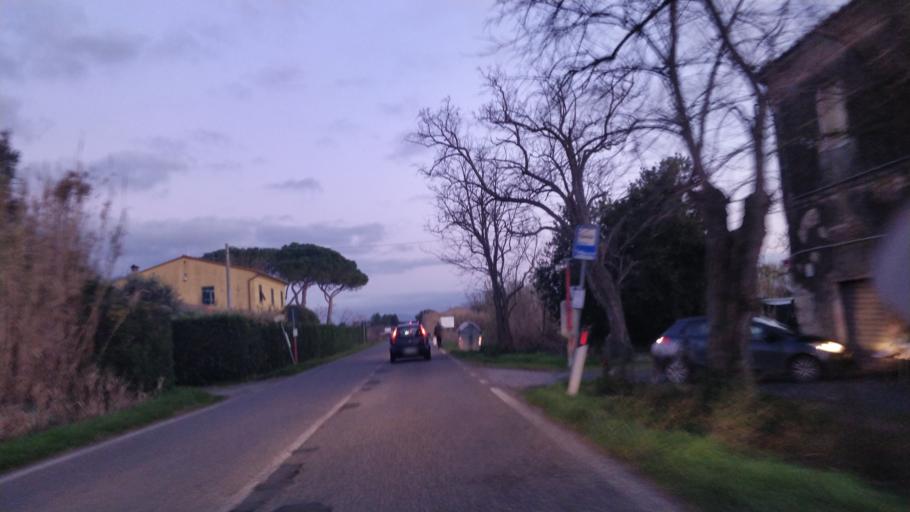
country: IT
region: Tuscany
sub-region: Provincia di Livorno
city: Vada
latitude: 43.3454
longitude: 10.4698
